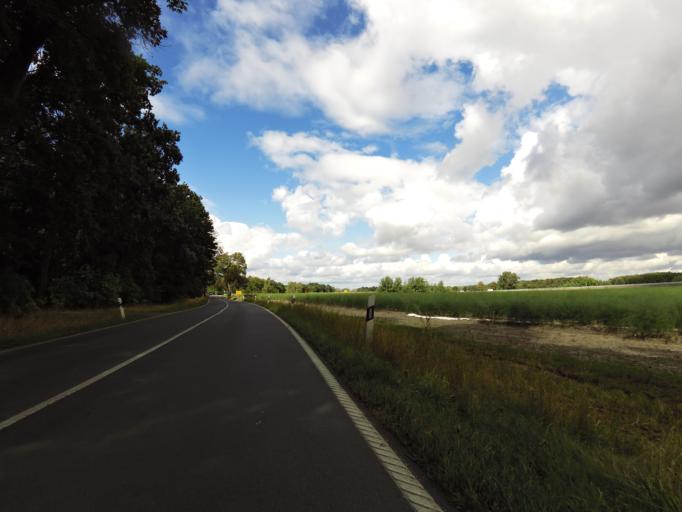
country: DE
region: Berlin
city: Lichtenrade
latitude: 52.3666
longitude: 13.3657
